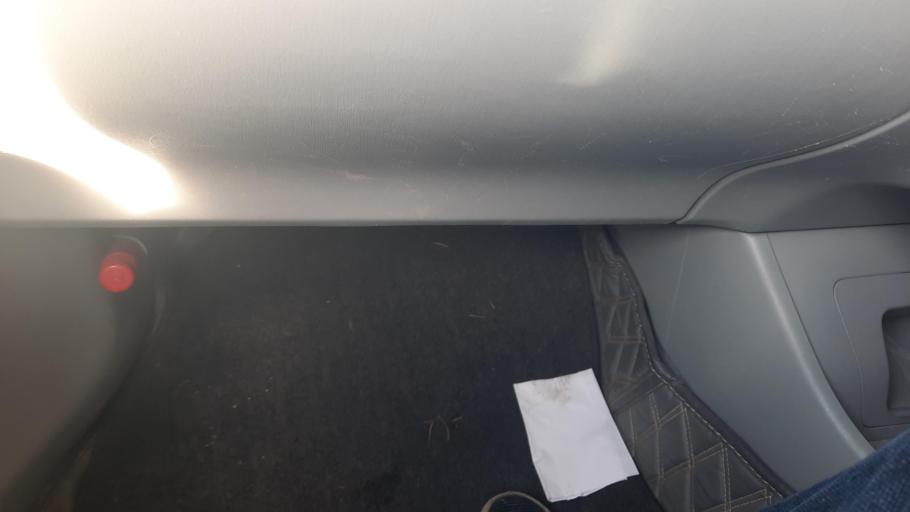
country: MN
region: Orhon
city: Erdenet
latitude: 49.0360
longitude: 104.0515
